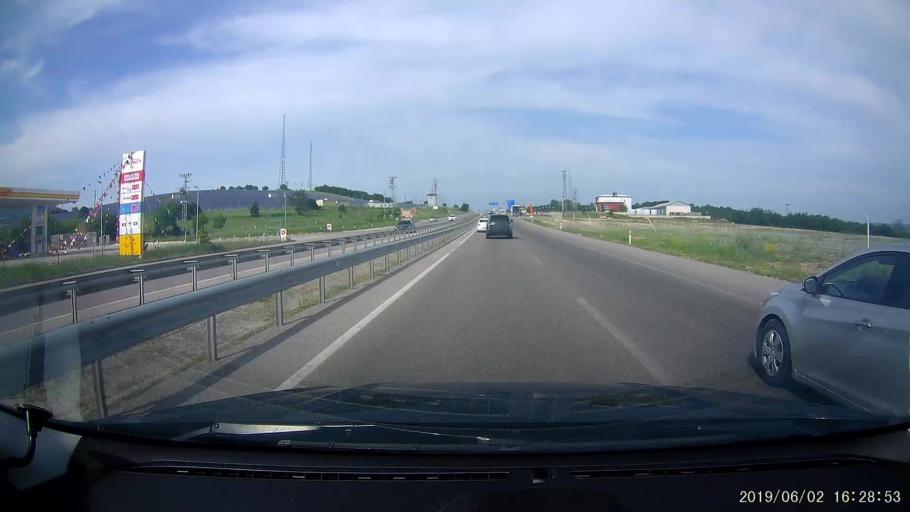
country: TR
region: Samsun
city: Ladik
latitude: 41.0092
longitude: 35.8577
